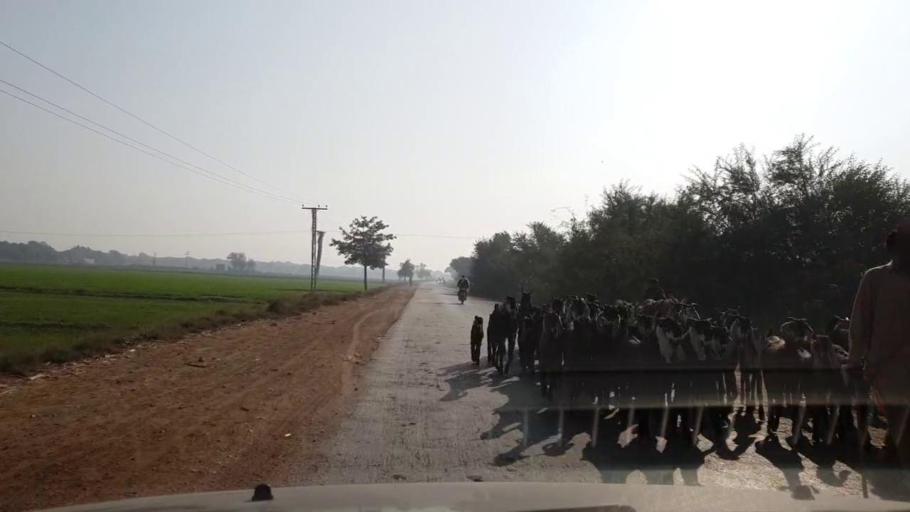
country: PK
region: Sindh
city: Matiari
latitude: 25.5934
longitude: 68.4701
